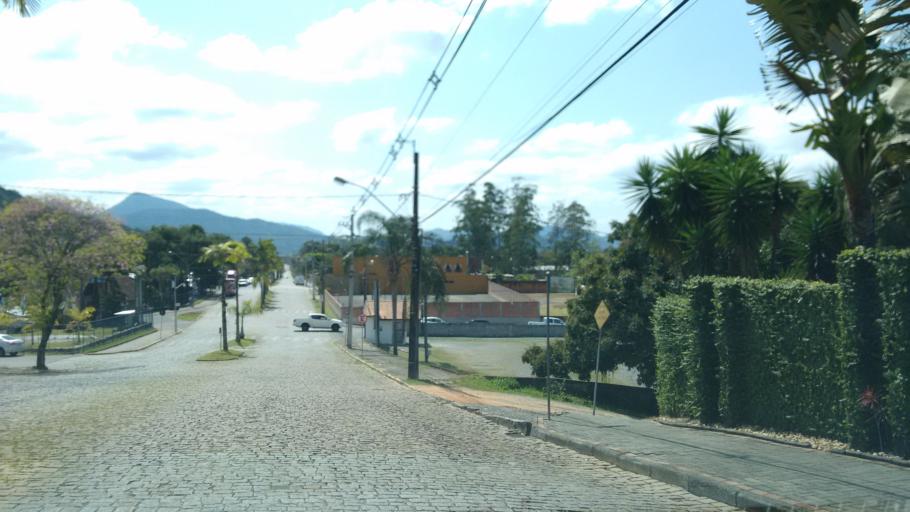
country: BR
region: Santa Catarina
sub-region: Pomerode
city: Pomerode
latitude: -26.7480
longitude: -49.1756
